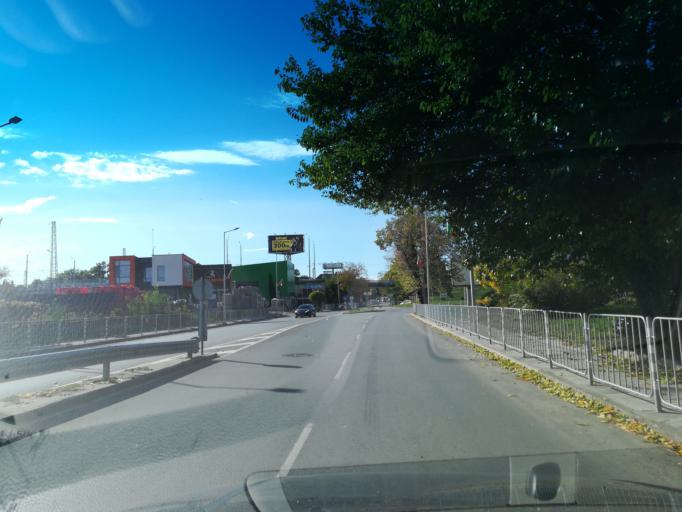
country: BG
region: Stara Zagora
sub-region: Obshtina Stara Zagora
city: Stara Zagora
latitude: 42.4210
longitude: 25.6379
